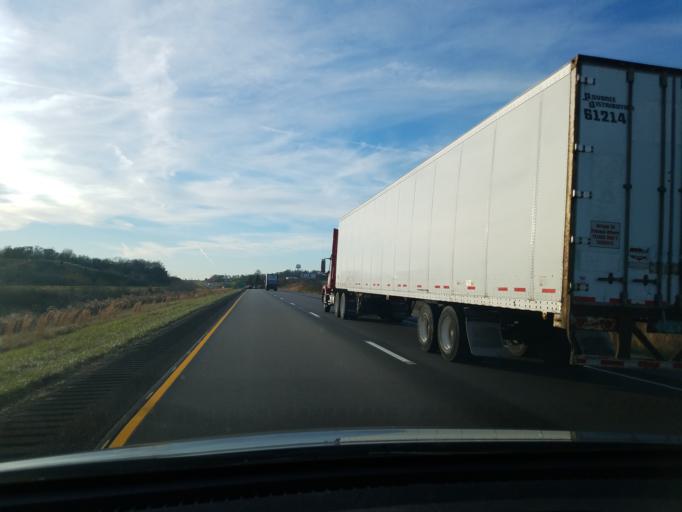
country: US
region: Indiana
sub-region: Dubois County
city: Ferdinand
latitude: 38.2042
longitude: -86.8419
